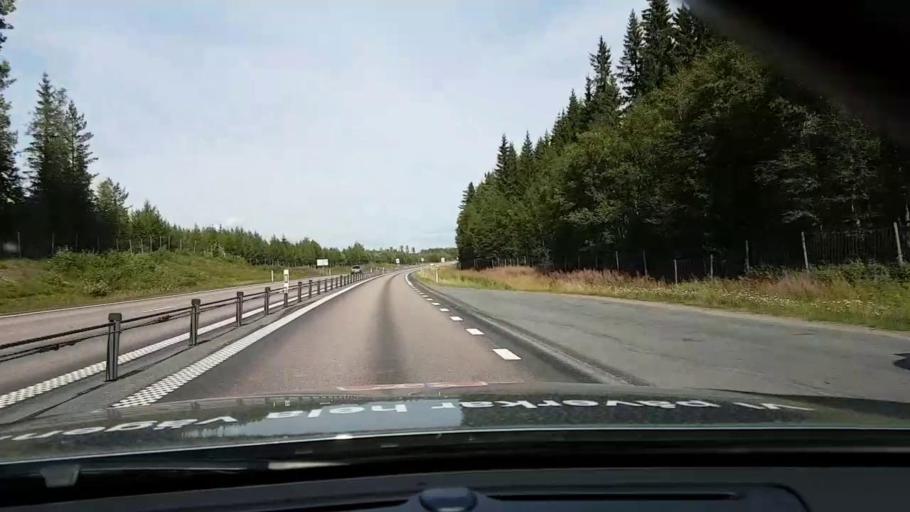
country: SE
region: Vaesternorrland
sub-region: OErnskoeldsviks Kommun
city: Husum
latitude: 63.4402
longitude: 19.2130
